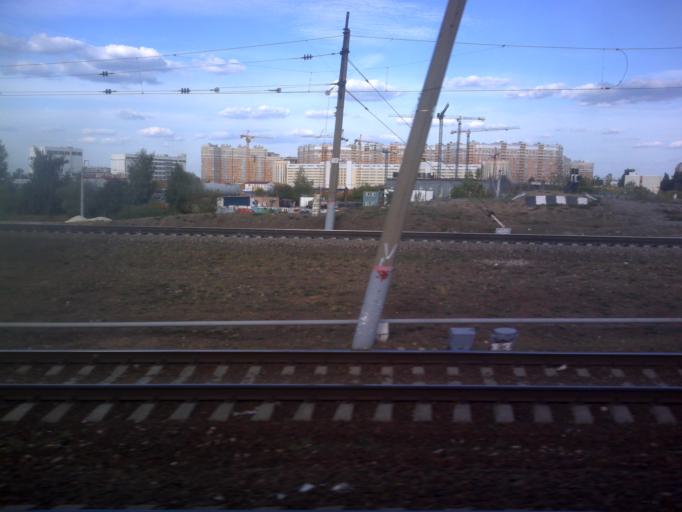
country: RU
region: Moskovskaya
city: Biryulevo Zapadnoye
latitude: 55.6023
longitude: 37.6481
